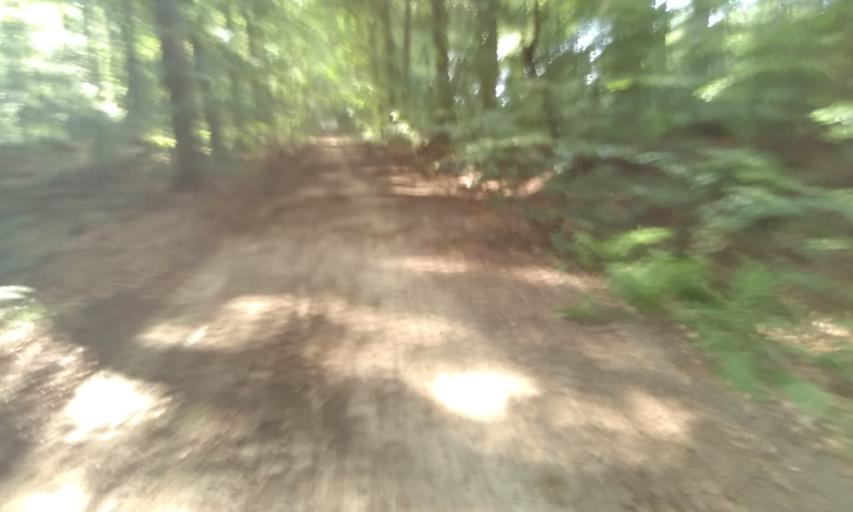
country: DE
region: Lower Saxony
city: Nottensdorf
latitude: 53.4765
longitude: 9.6422
